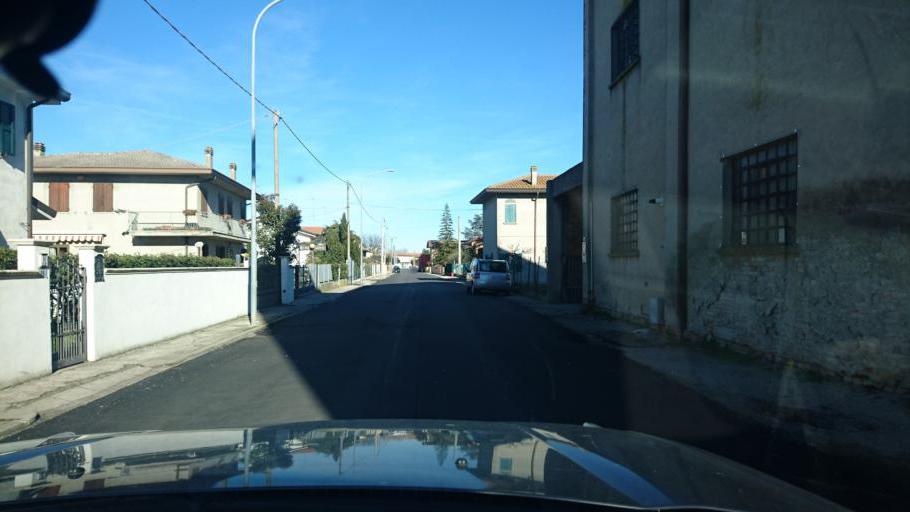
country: IT
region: Veneto
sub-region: Provincia di Rovigo
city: Ariano
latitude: 44.9471
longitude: 12.1194
